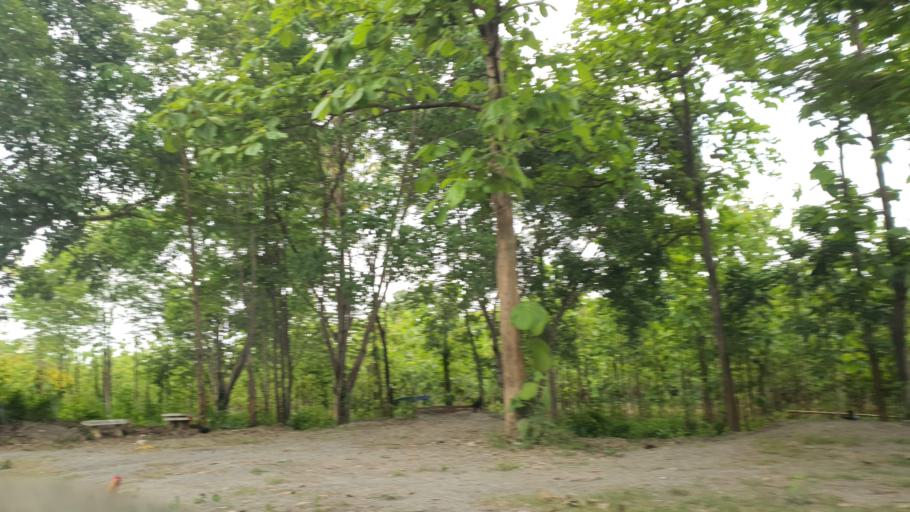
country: TH
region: Sukhothai
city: Thung Saliam
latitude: 17.2639
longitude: 99.5364
